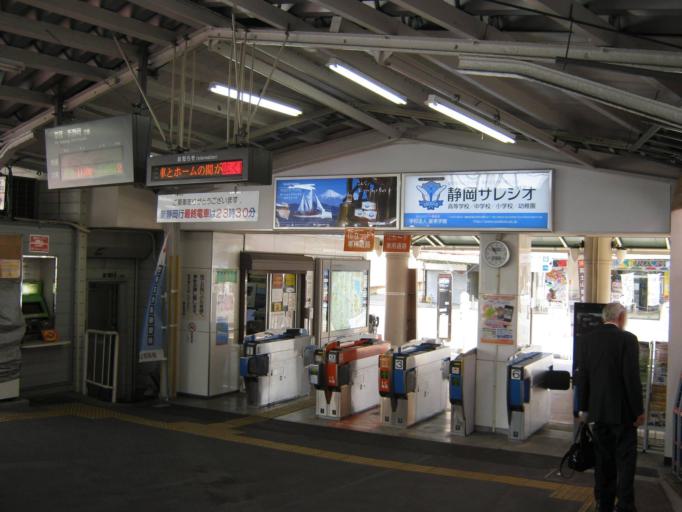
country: JP
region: Shizuoka
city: Shizuoka-shi
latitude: 35.0171
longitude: 138.4878
